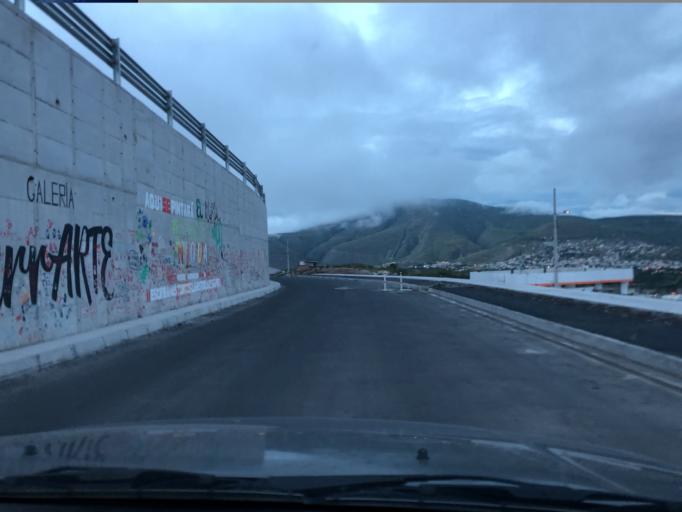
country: EC
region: Imbabura
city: Ibarra
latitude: 0.3711
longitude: -78.1291
